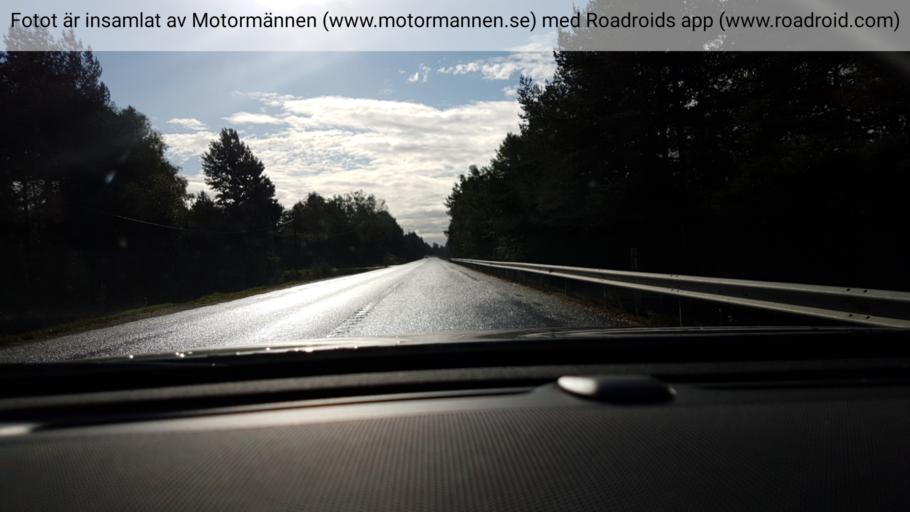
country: SE
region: Vaestra Goetaland
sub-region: Harryda Kommun
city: Hindas
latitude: 57.6713
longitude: 12.3569
